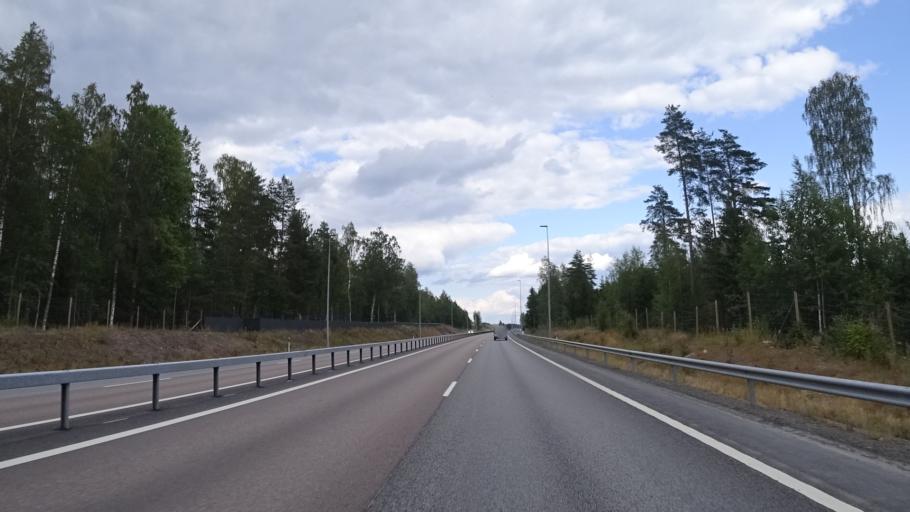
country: FI
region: South Karelia
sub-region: Lappeenranta
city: Luumaeki
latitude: 60.9361
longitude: 27.6768
